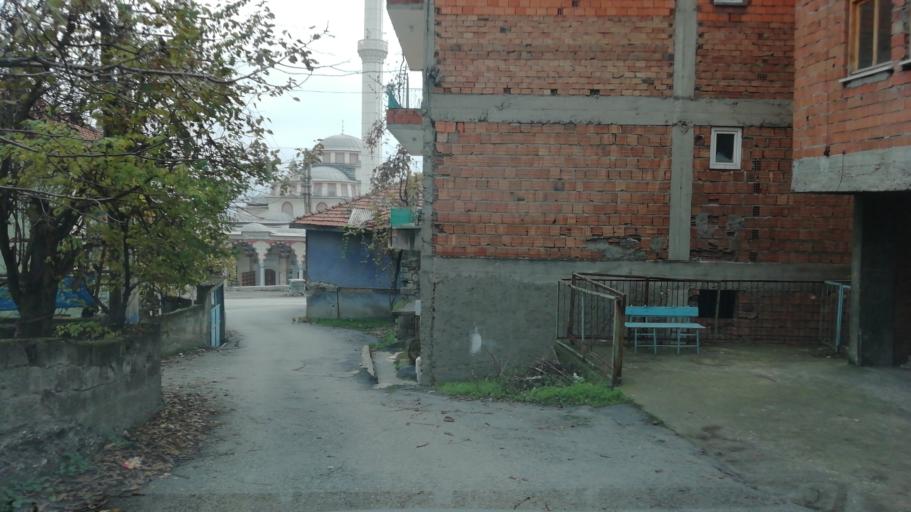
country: TR
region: Karabuk
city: Karabuk
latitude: 41.2271
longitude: 32.6217
